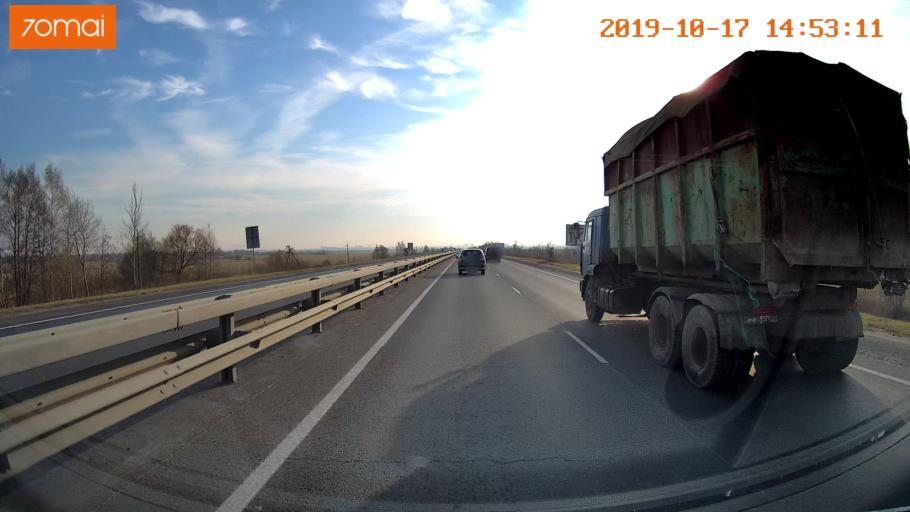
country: RU
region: Rjazan
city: Polyany
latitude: 54.6973
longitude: 39.8403
